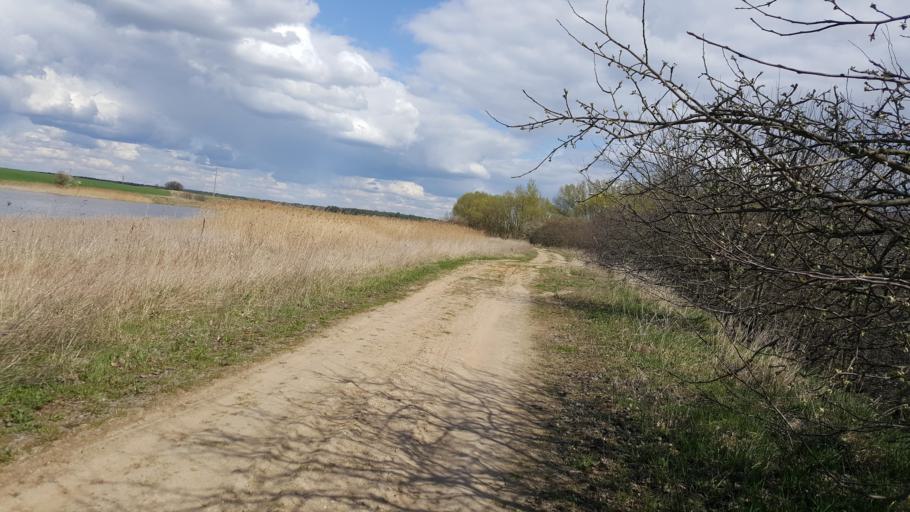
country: BY
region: Brest
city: Kamyanyets
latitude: 52.3720
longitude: 23.6520
